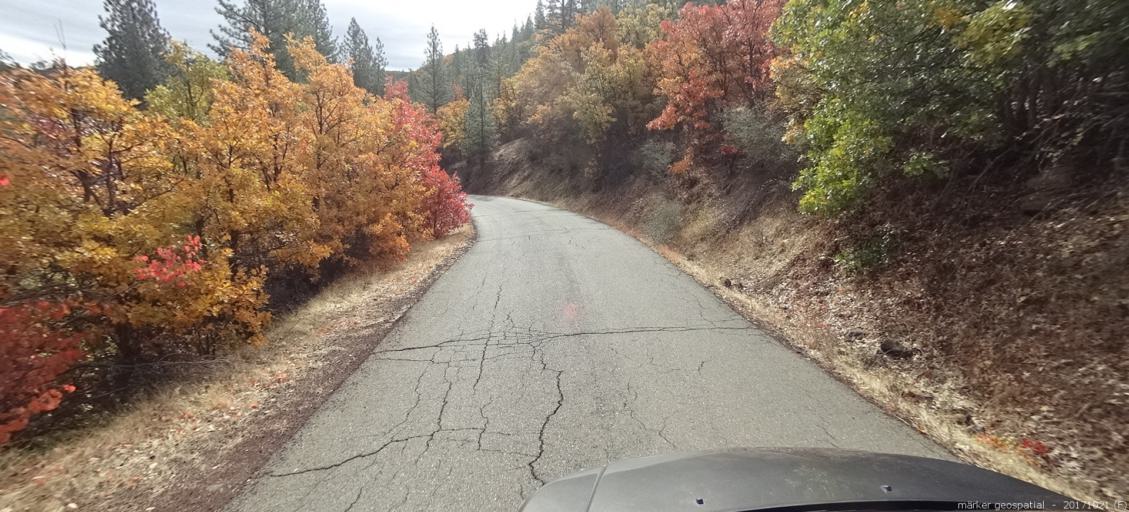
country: US
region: California
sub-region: Shasta County
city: Burney
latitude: 40.9594
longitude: -121.5534
